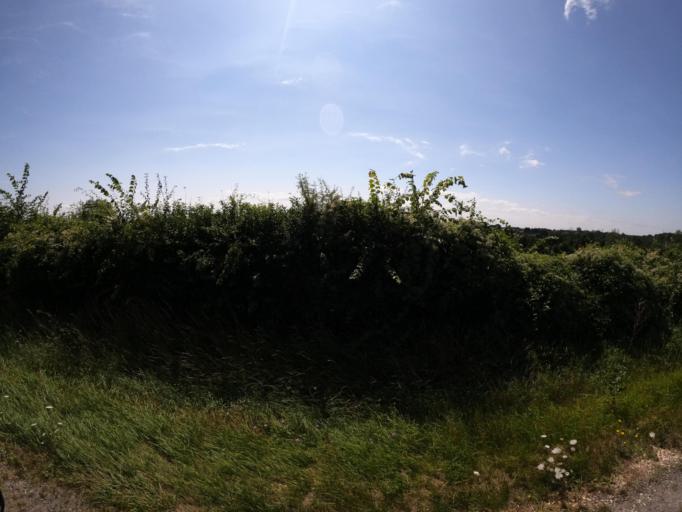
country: FR
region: Poitou-Charentes
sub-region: Departement de la Vienne
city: Savigne
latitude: 46.1590
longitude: 0.3506
